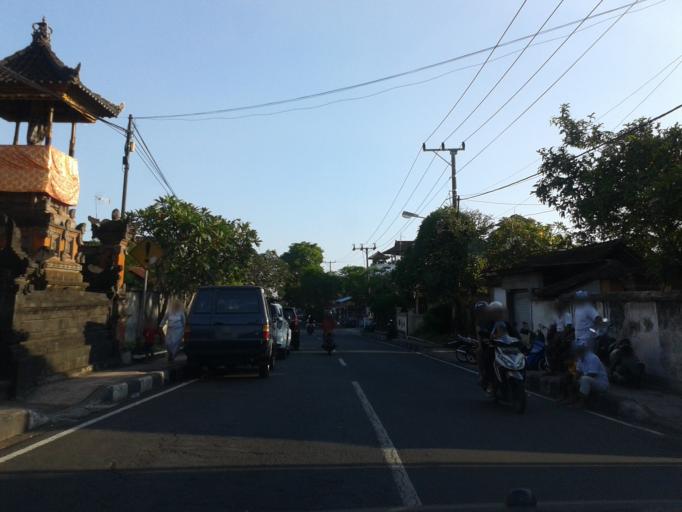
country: ID
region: Bali
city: Semarapura
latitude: -8.5410
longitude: 115.4027
